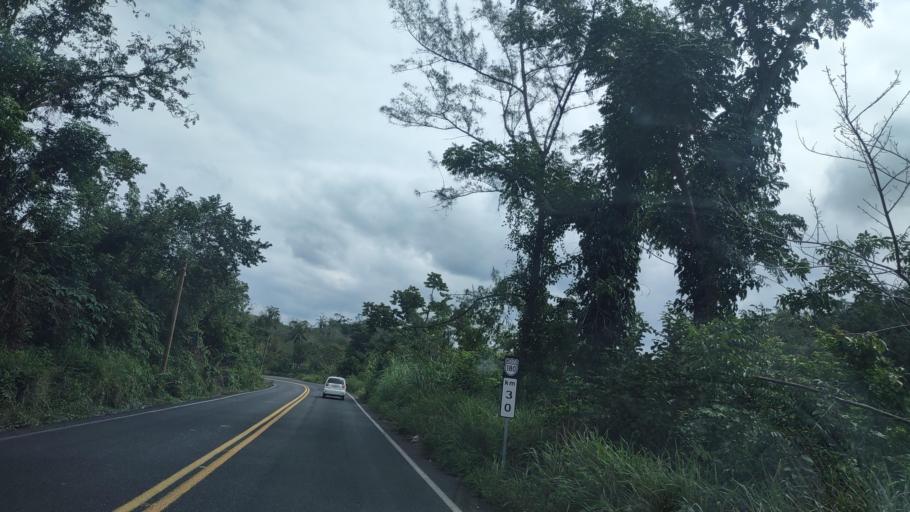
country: MX
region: Veracruz
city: Papantla de Olarte
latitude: 20.4627
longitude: -97.2694
